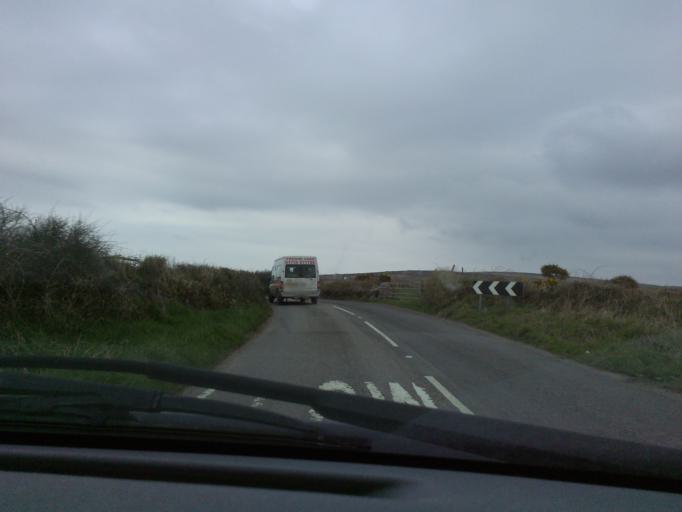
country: GB
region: England
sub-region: Cornwall
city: Saint Just
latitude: 50.0969
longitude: -5.6647
